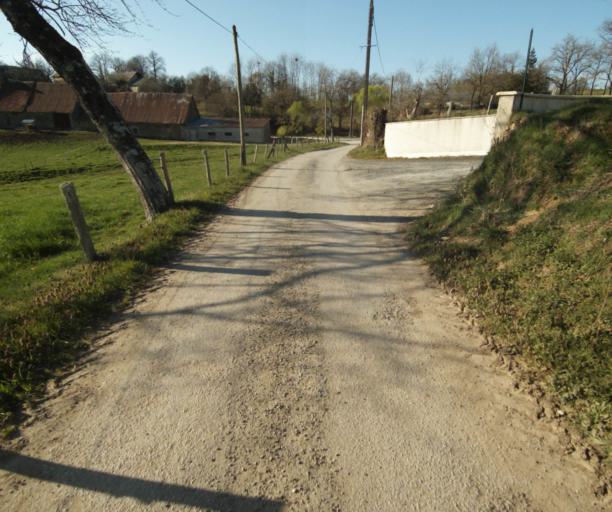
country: FR
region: Limousin
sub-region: Departement de la Correze
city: Chamboulive
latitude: 45.4969
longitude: 1.7286
